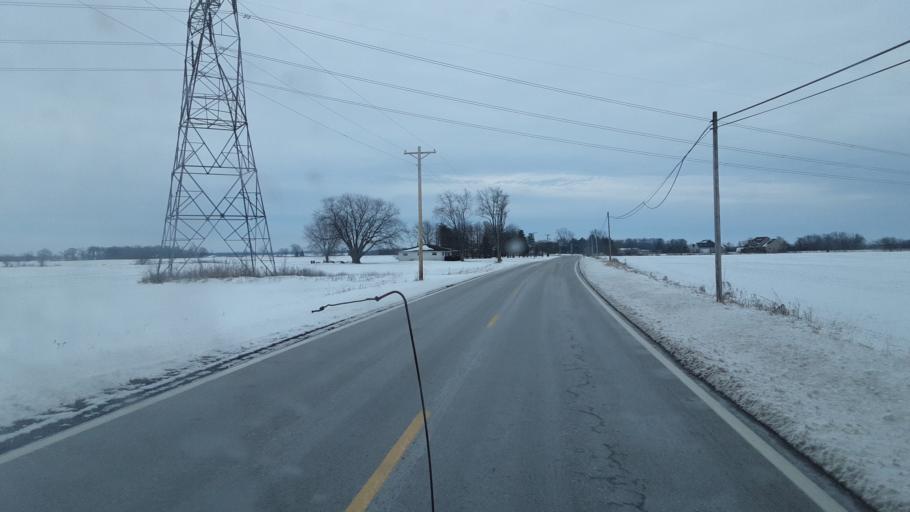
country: US
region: Ohio
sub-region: Pickaway County
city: Williamsport
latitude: 39.6699
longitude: -83.1667
